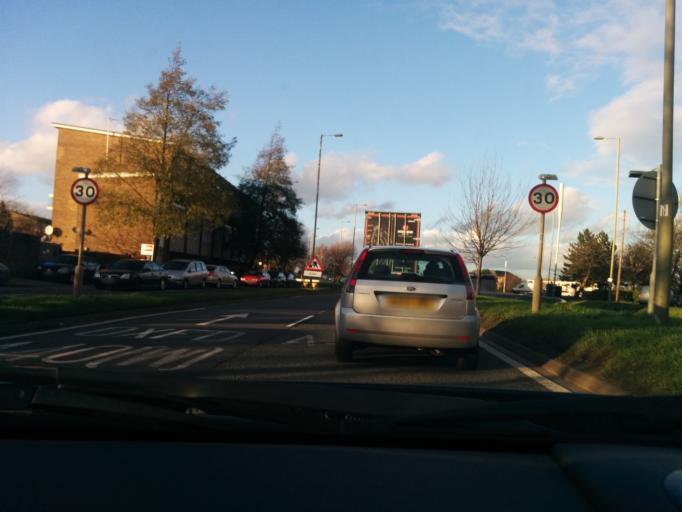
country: GB
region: England
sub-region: Oxfordshire
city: Cowley
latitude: 51.7615
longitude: -1.1962
